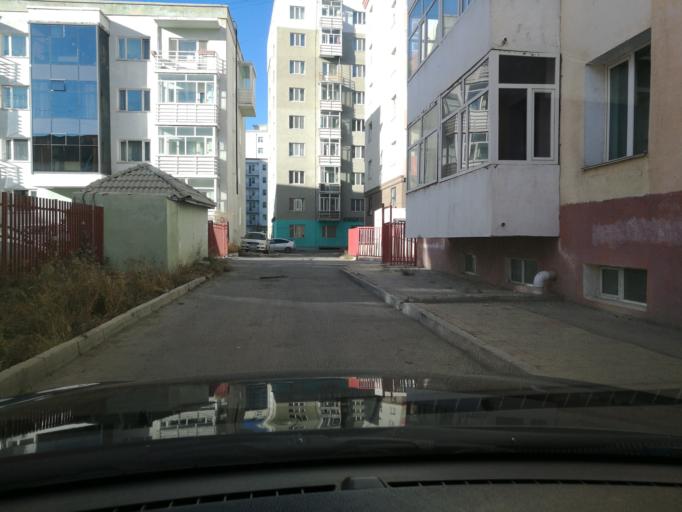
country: MN
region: Ulaanbaatar
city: Ulaanbaatar
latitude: 47.8901
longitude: 106.9018
